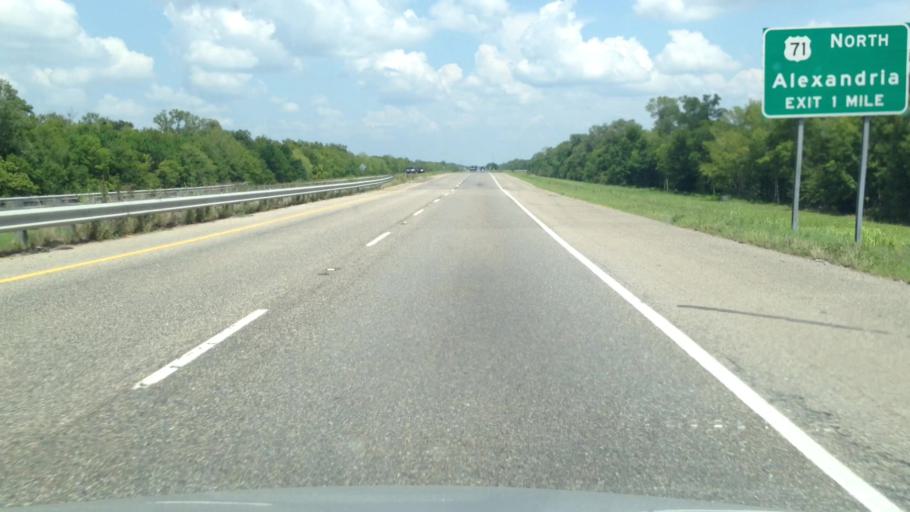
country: US
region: Louisiana
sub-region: Saint Landry Parish
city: Krotz Springs
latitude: 30.5474
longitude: -91.8248
